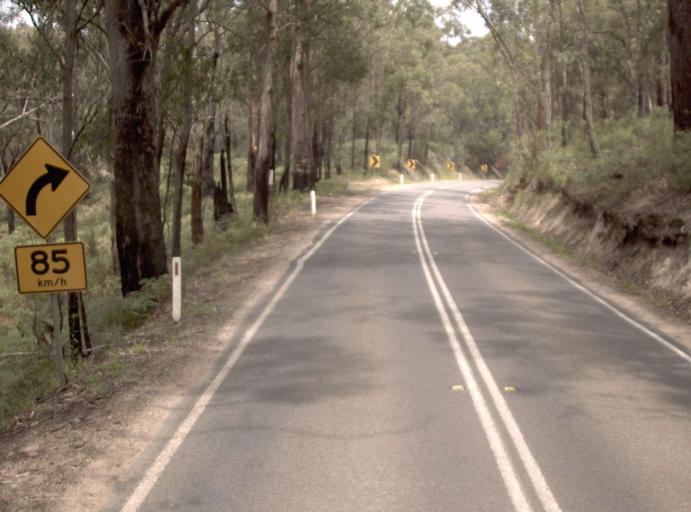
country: AU
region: Victoria
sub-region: Latrobe
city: Traralgon
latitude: -38.4207
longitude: 146.7476
